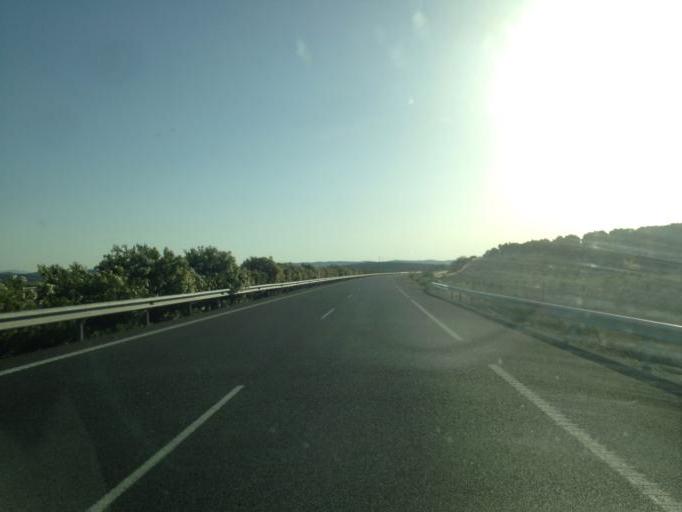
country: ES
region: Andalusia
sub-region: Provincia de Malaga
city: Villanueva del Trabuco
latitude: 37.0610
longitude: -4.3474
